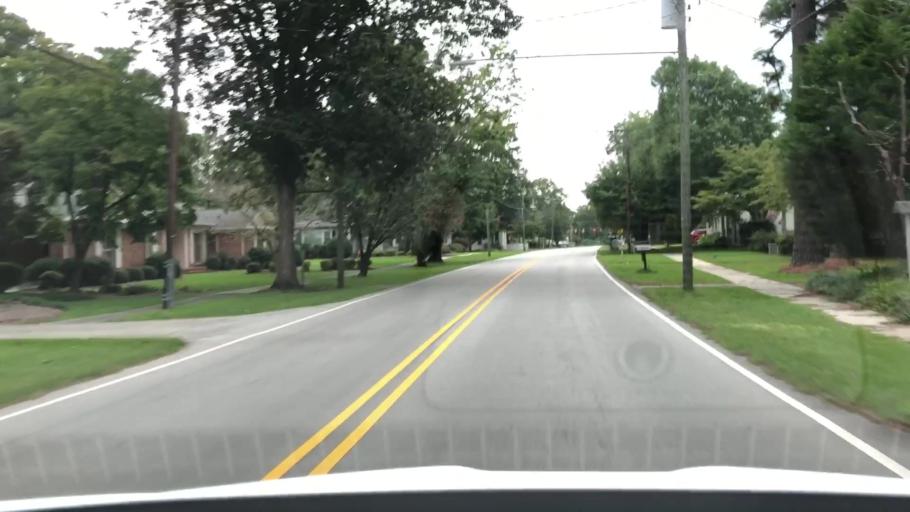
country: US
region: North Carolina
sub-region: Jones County
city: Trenton
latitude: 35.0611
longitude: -77.3548
